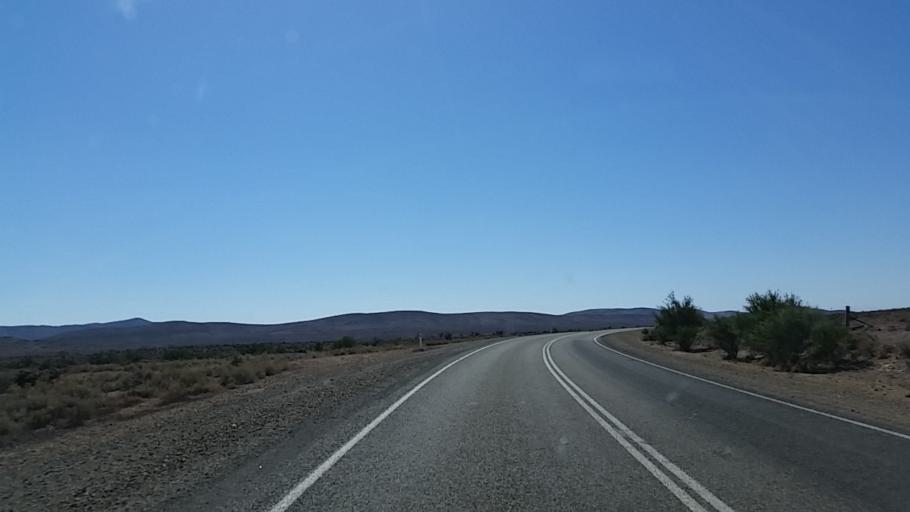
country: AU
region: South Australia
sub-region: Flinders Ranges
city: Quorn
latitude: -32.2471
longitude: 138.5134
